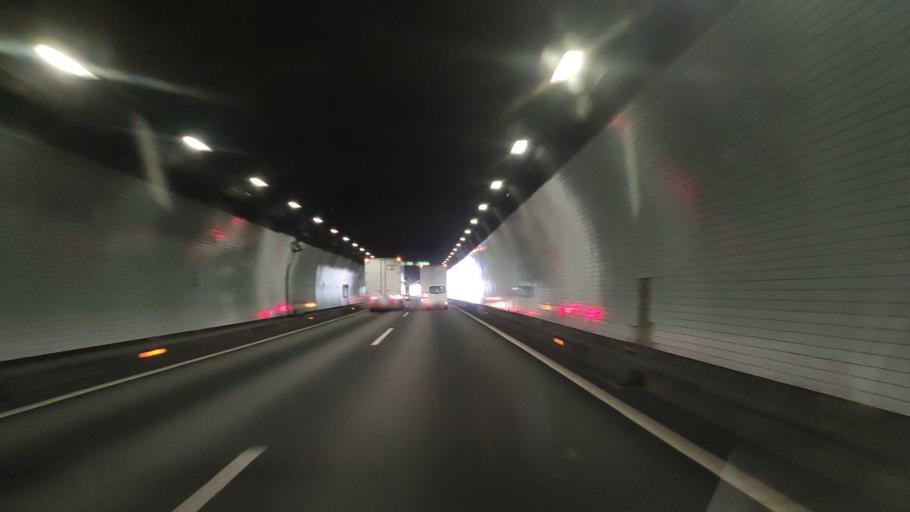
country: JP
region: Tokyo
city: Fussa
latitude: 35.7471
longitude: 139.2819
